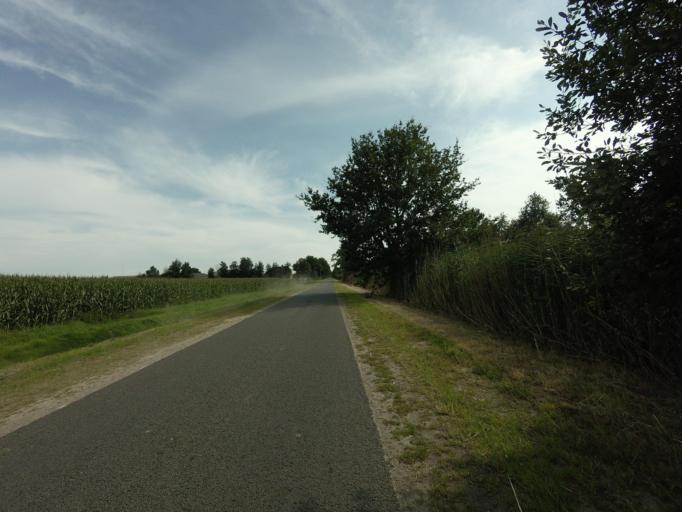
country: NL
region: Drenthe
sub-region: Gemeente Coevorden
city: Coevorden
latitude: 52.6896
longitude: 6.7097
